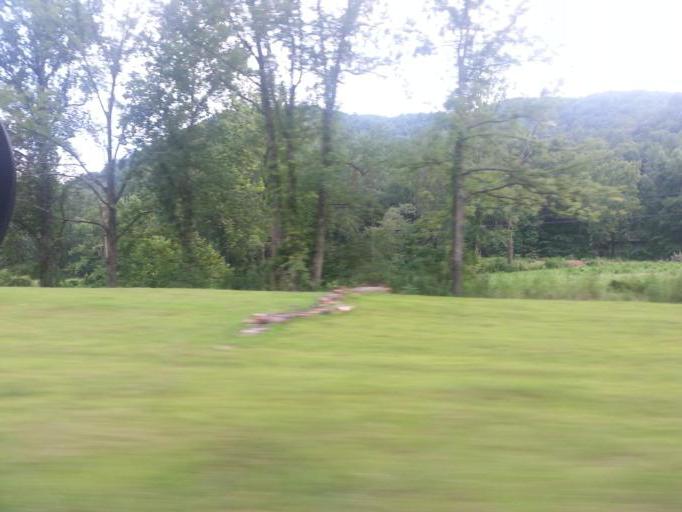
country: US
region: Tennessee
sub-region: Campbell County
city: Caryville
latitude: 36.2073
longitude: -84.3114
